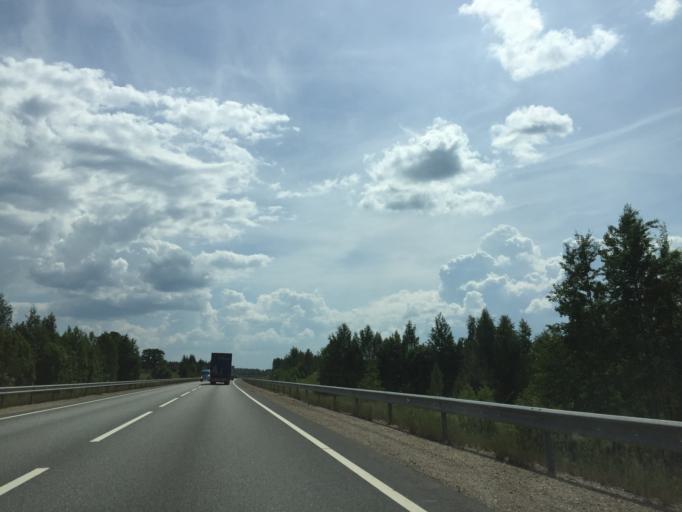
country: LV
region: Skriveri
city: Skriveri
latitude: 56.7624
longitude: 25.1040
